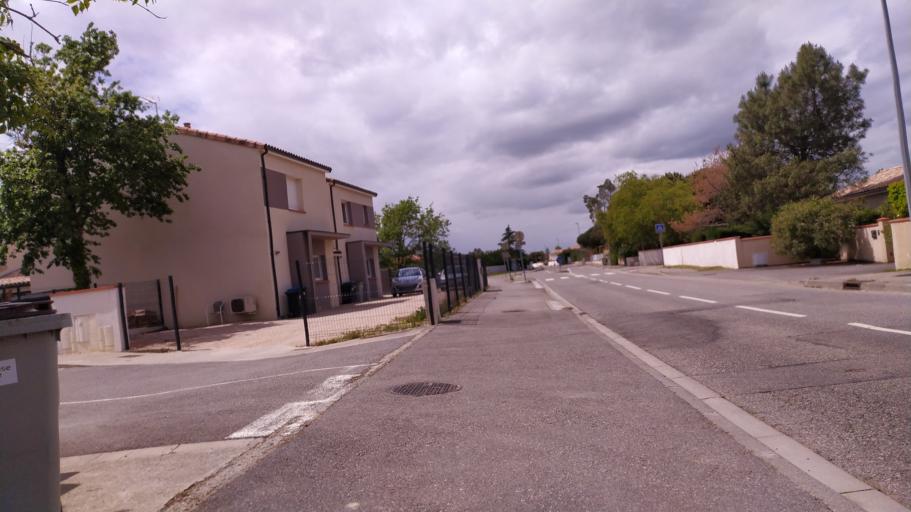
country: FR
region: Midi-Pyrenees
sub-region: Departement de la Haute-Garonne
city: Plaisance-du-Touch
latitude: 43.5814
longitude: 1.2985
